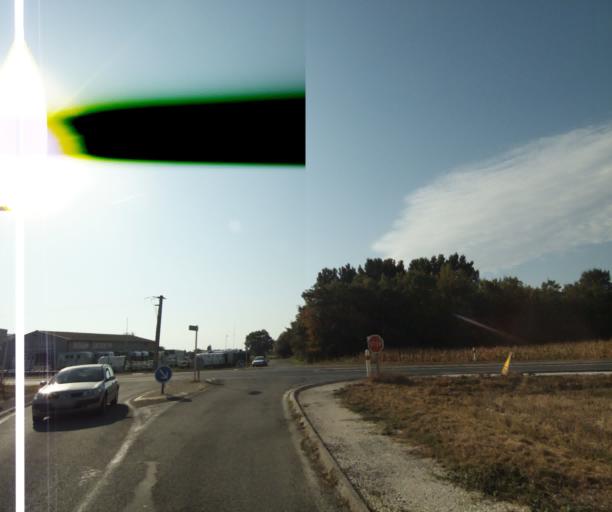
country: FR
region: Poitou-Charentes
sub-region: Departement de la Charente-Maritime
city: Cabariot
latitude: 45.9603
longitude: -0.8388
